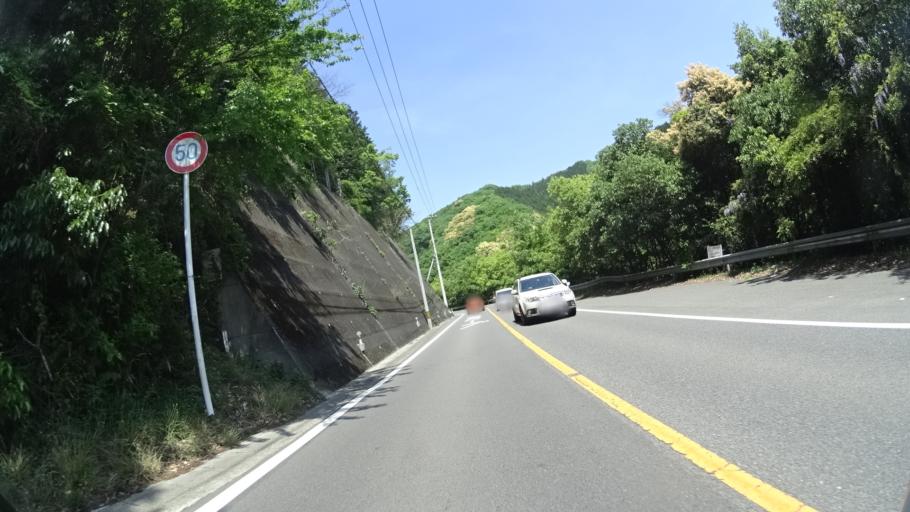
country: JP
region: Ehime
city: Hojo
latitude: 33.9839
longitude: 132.9077
